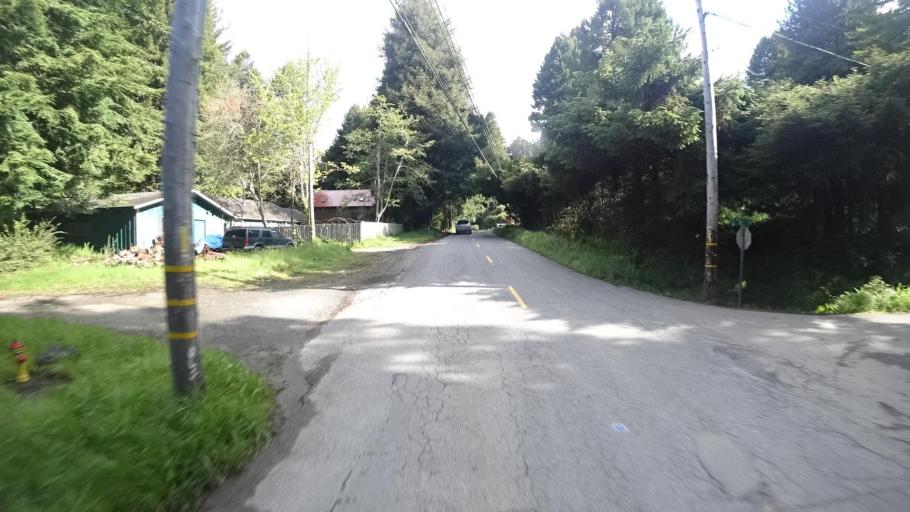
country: US
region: California
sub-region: Humboldt County
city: Westhaven-Moonstone
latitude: 41.0379
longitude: -124.1076
